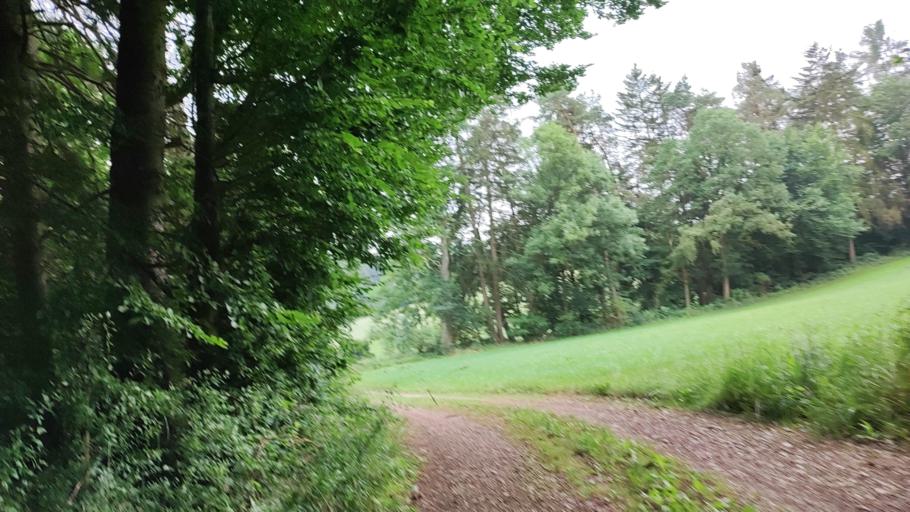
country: DE
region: Bavaria
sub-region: Swabia
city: Welden
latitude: 48.4555
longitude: 10.6782
